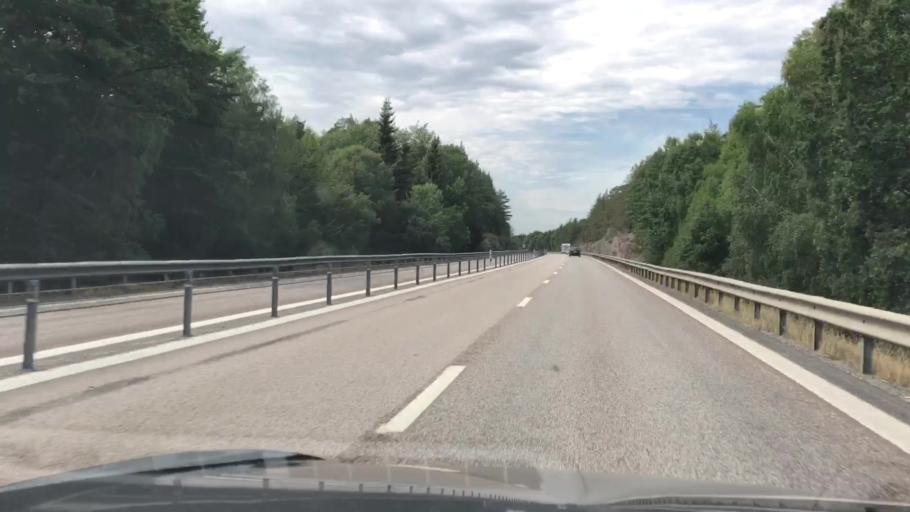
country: SE
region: Blekinge
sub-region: Ronneby Kommun
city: Brakne-Hoby
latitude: 56.2208
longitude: 15.1503
